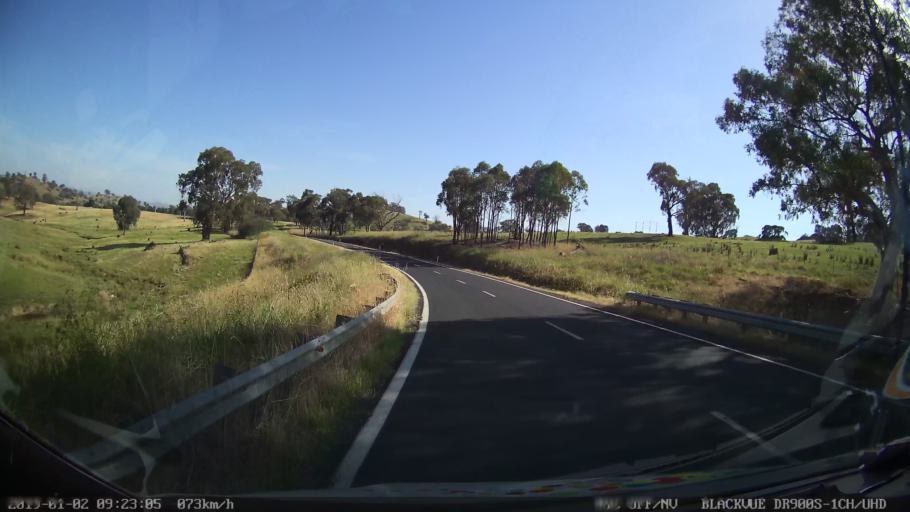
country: AU
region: New South Wales
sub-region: Tumut Shire
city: Tumut
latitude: -35.3914
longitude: 148.2980
